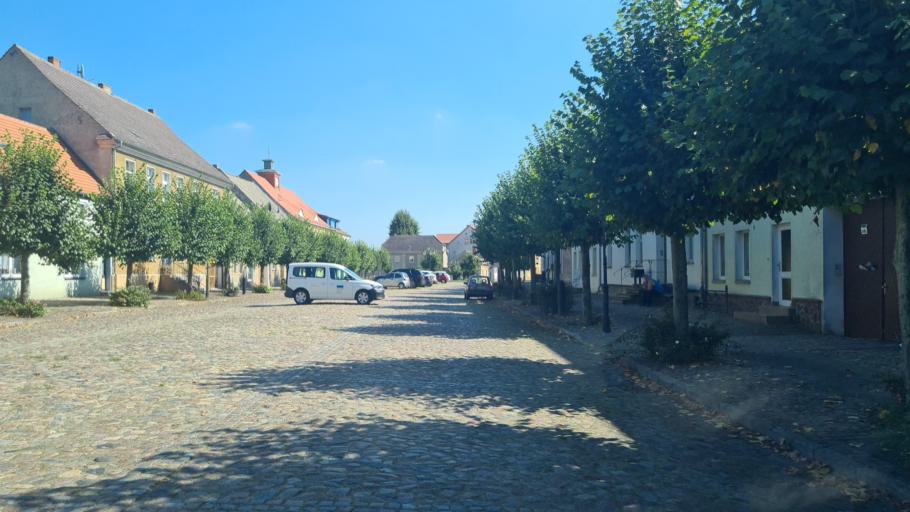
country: DE
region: Brandenburg
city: Friesack
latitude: 52.7417
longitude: 12.5808
